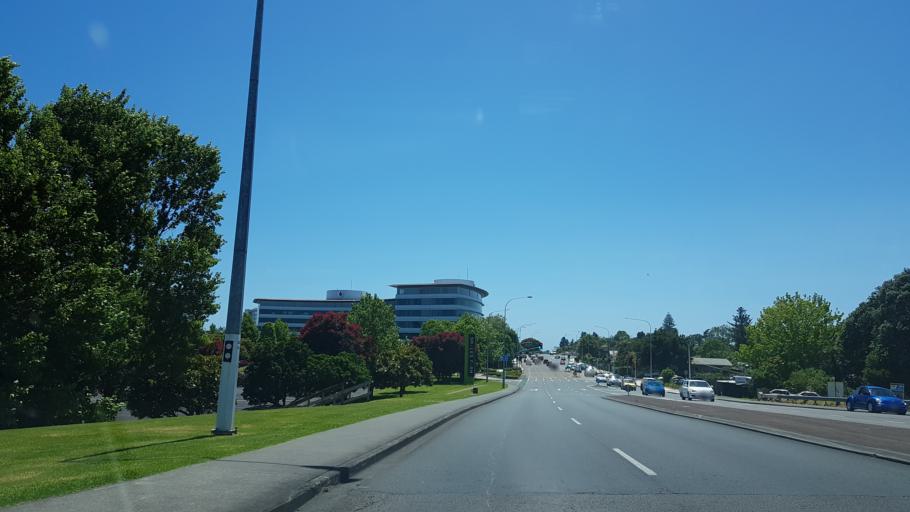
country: NZ
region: Auckland
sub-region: Auckland
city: North Shore
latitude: -36.7877
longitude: 174.7534
